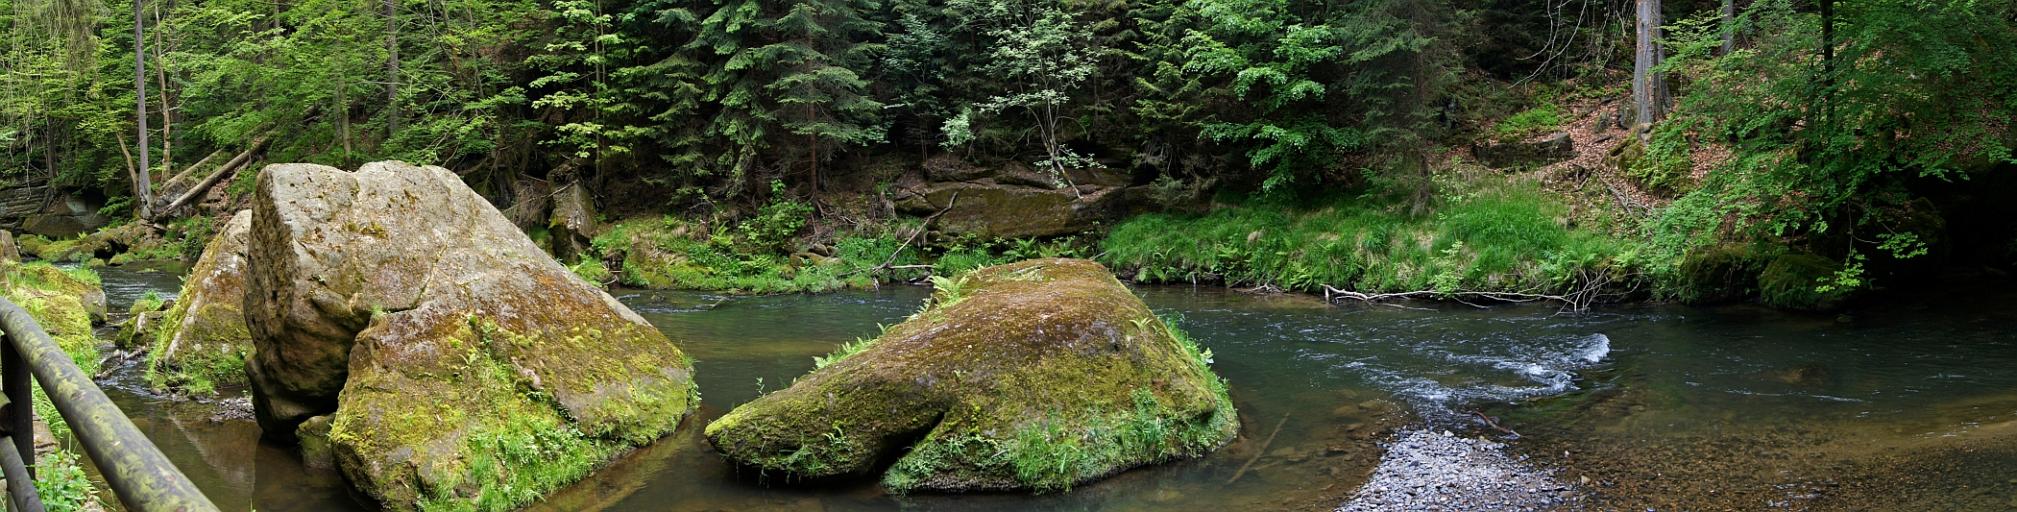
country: DE
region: Saxony
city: Sebnitz
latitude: 50.8699
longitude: 14.2808
